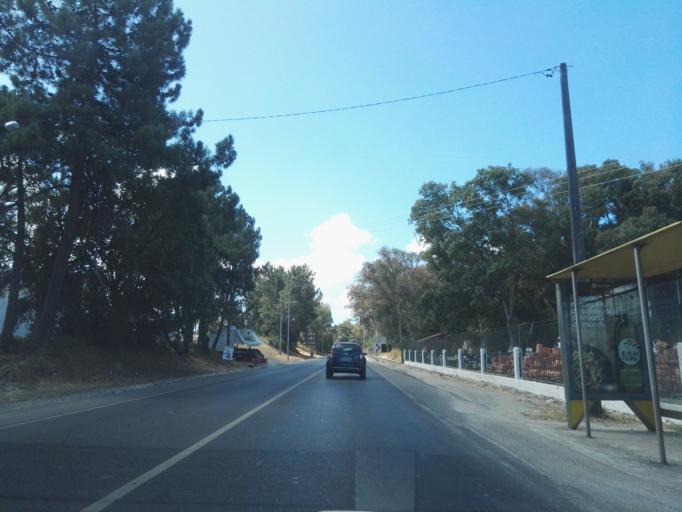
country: PT
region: Setubal
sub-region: Seixal
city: Arrentela
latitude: 38.5965
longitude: -9.1062
